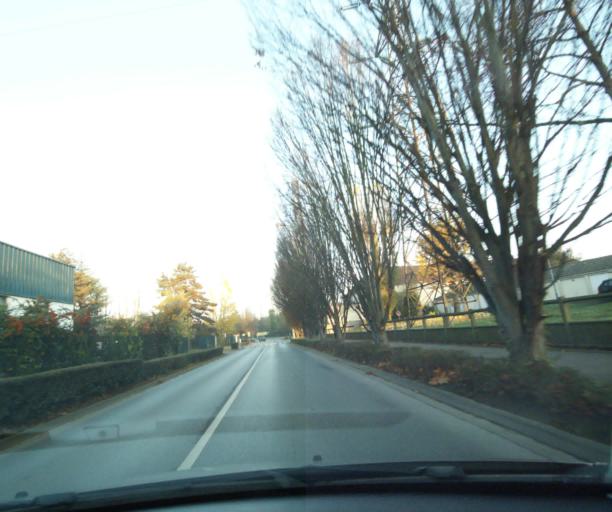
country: FR
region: Ile-de-France
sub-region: Departement de Seine-Saint-Denis
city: Gagny
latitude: 48.8730
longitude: 2.5326
